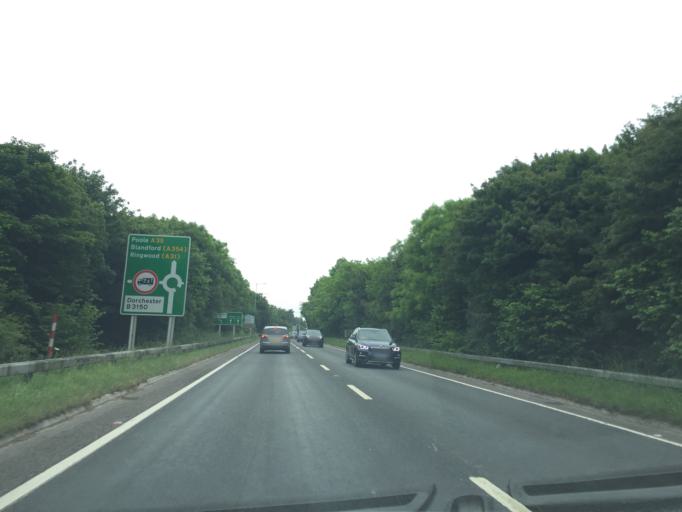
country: GB
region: England
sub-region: Dorset
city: Dorchester
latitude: 50.7177
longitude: -2.4152
